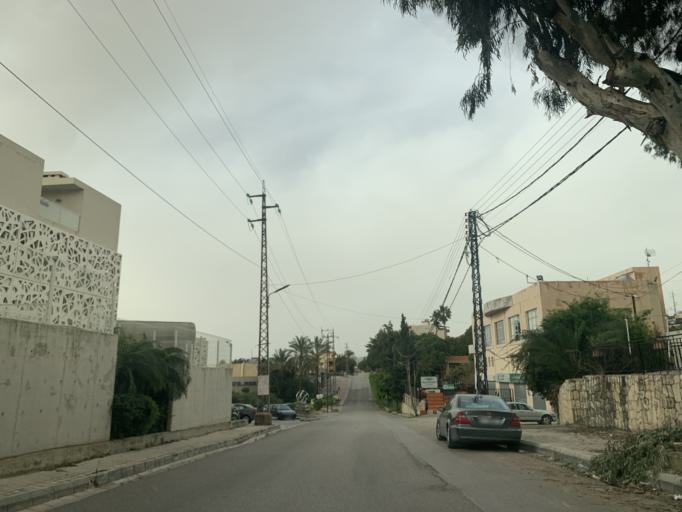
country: LB
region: Mont-Liban
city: Jbail
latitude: 34.0908
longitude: 35.6508
